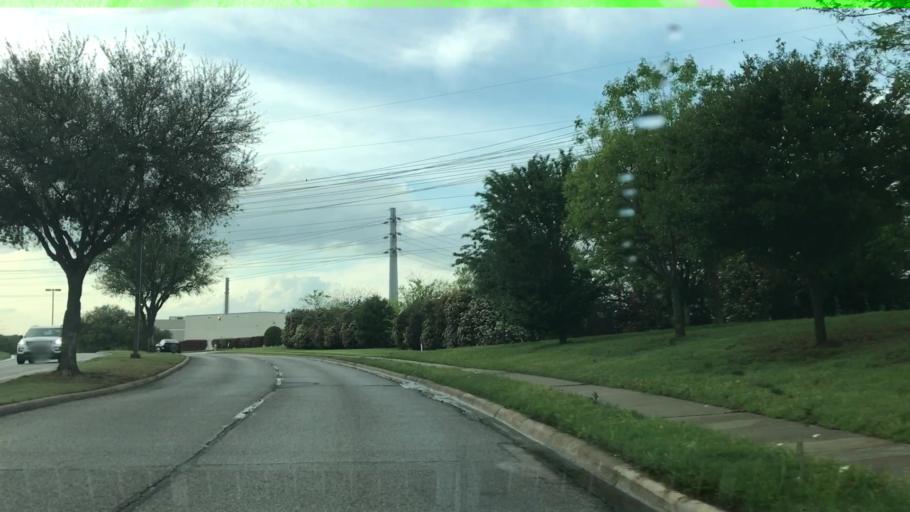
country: US
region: Texas
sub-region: Dallas County
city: Irving
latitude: 32.8680
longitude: -96.9775
